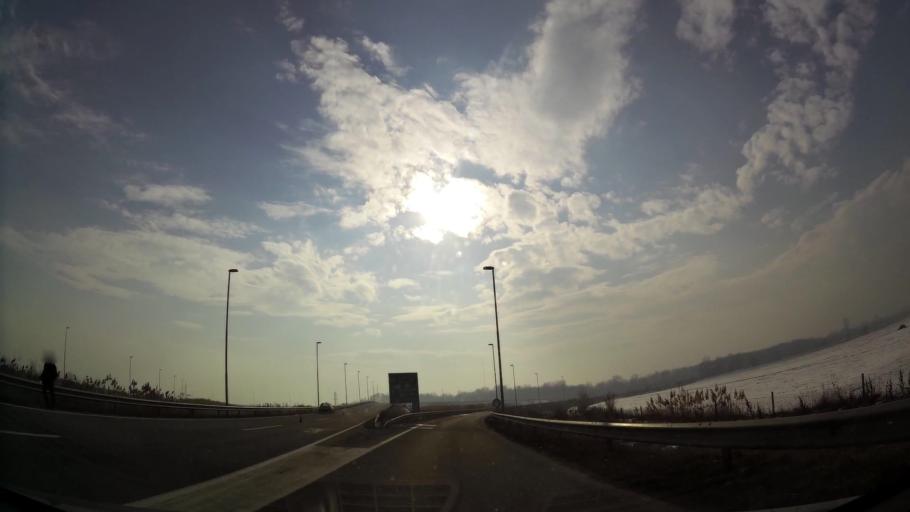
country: MK
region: Ilinden
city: Jurumleri
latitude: 41.9984
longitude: 21.5324
